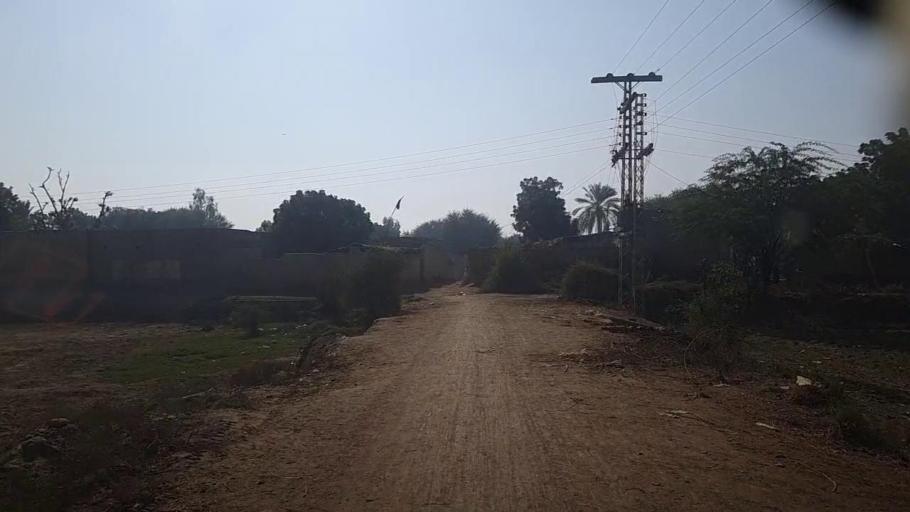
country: PK
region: Sindh
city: Kandiari
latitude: 27.0208
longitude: 68.5078
